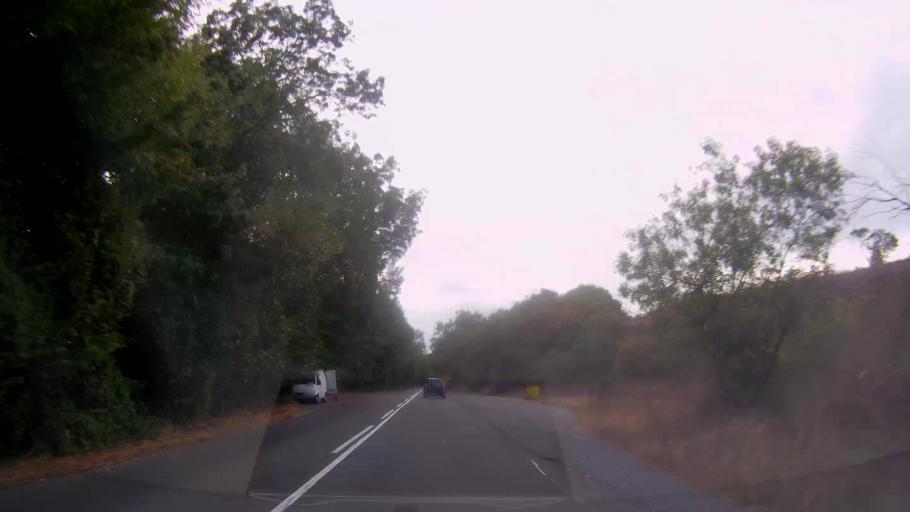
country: BG
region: Burgas
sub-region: Obshtina Primorsko
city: Primorsko
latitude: 42.3086
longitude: 27.7238
